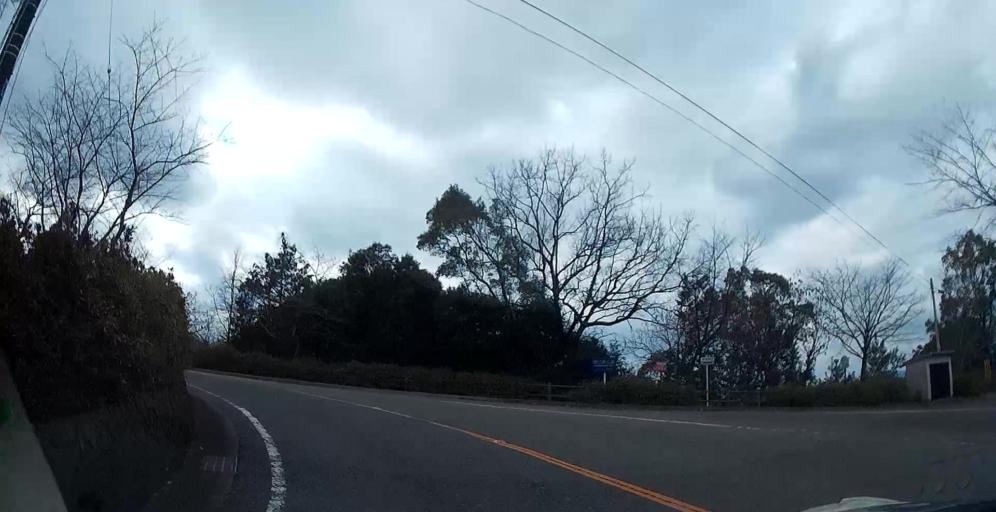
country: JP
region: Kumamoto
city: Yatsushiro
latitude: 32.3723
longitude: 130.5026
